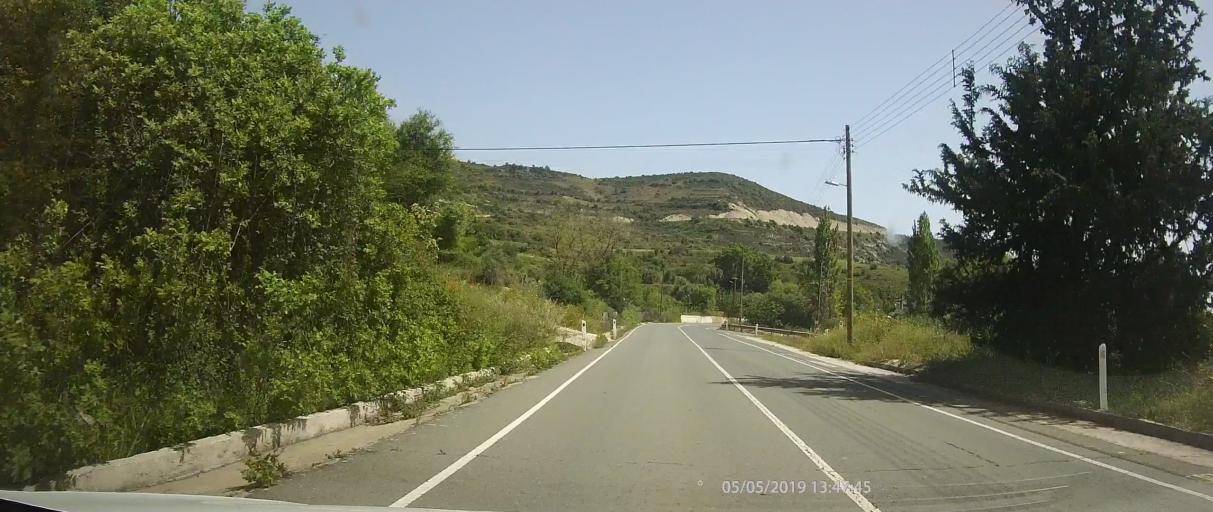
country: CY
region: Limassol
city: Pachna
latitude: 34.8633
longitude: 32.7559
